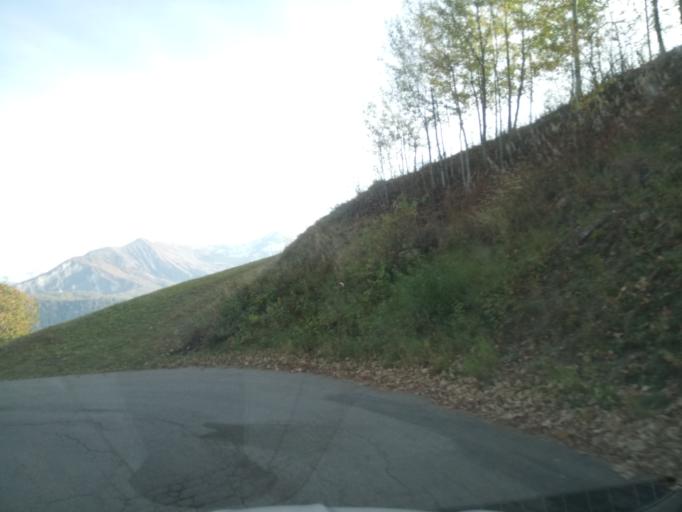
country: FR
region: Rhone-Alpes
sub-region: Departement de la Savoie
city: Saint-Jean-de-Maurienne
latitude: 45.2808
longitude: 6.3034
